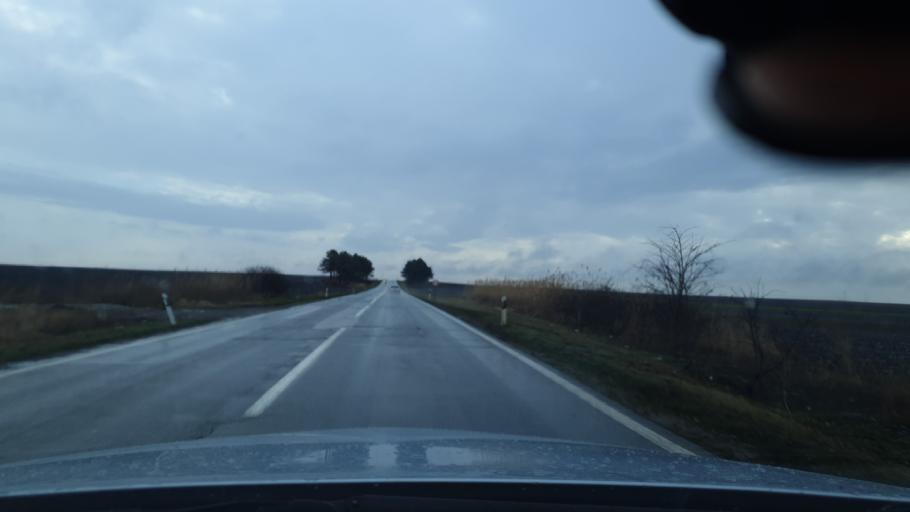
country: RS
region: Autonomna Pokrajina Vojvodina
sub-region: Juznobanatski Okrug
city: Kovin
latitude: 44.8320
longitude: 20.8277
